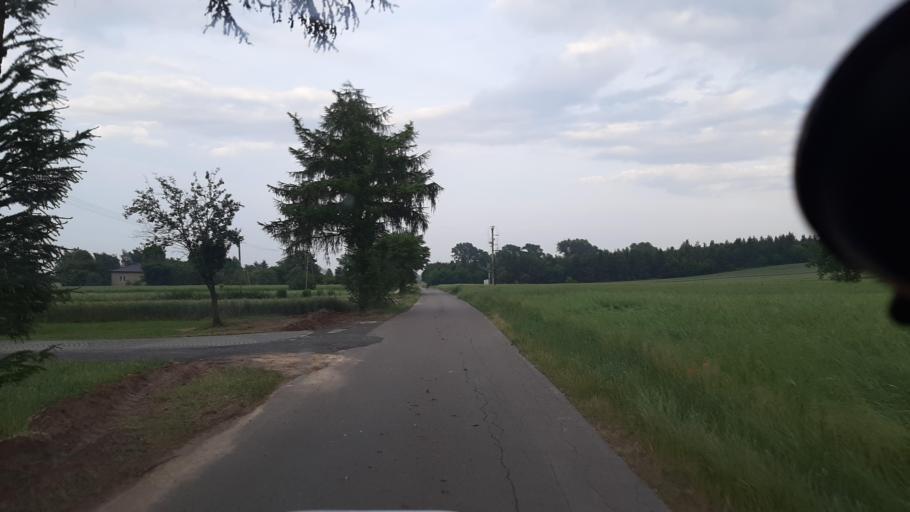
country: PL
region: Lublin Voivodeship
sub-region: Powiat lubelski
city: Garbow
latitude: 51.3507
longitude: 22.3599
